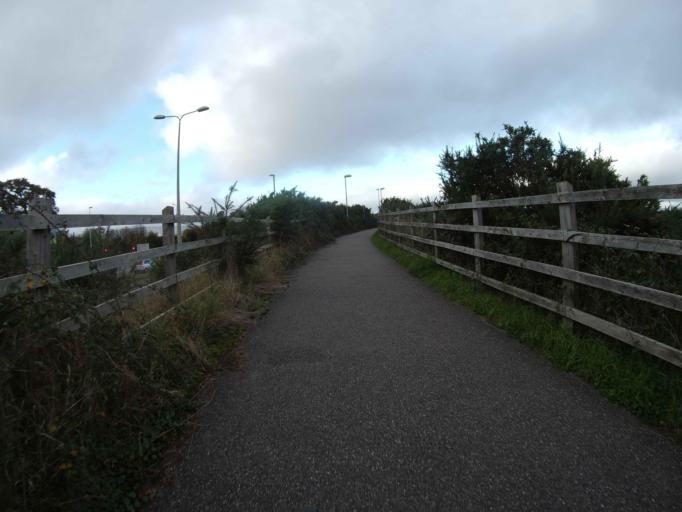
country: GB
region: England
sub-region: Devon
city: Heavitree
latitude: 50.7071
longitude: -3.4799
